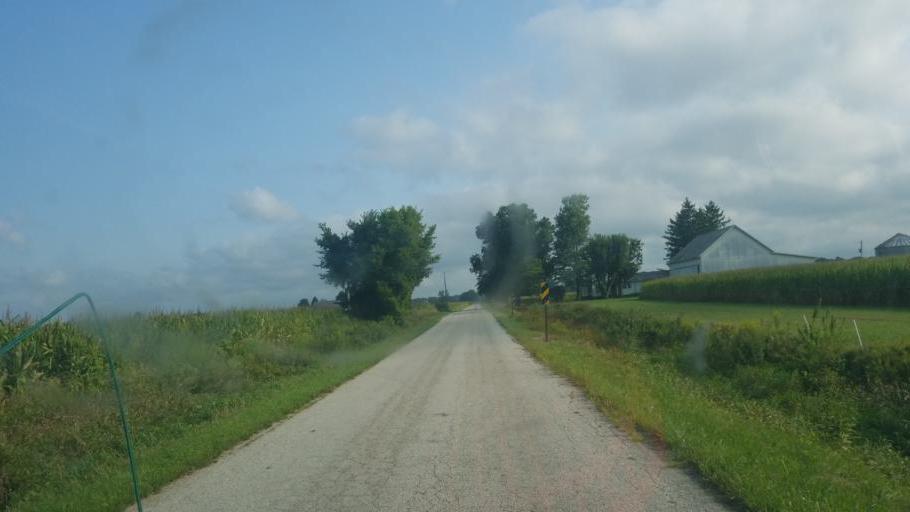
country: US
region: Ohio
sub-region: Delaware County
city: Ashley
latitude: 40.4763
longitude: -83.0075
